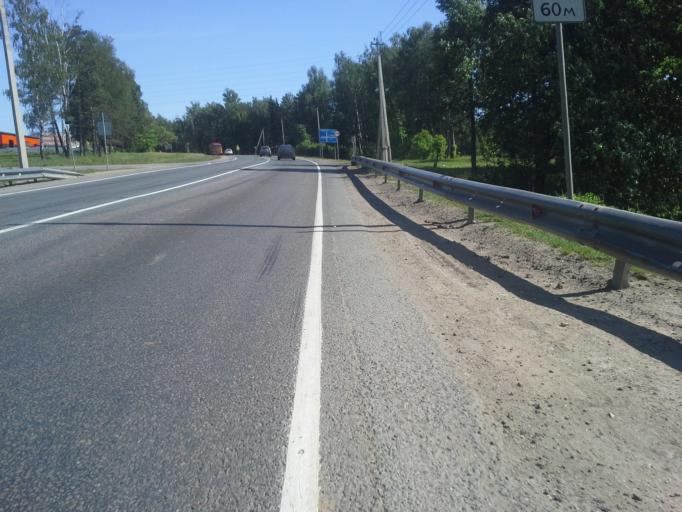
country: RU
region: Moskovskaya
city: Troitsk
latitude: 55.4085
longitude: 37.2009
